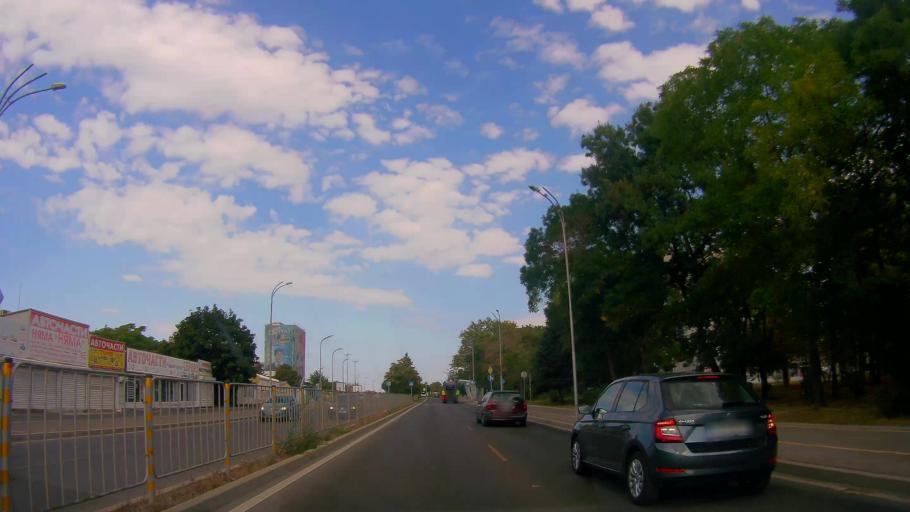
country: BG
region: Burgas
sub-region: Obshtina Burgas
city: Burgas
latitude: 42.5189
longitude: 27.4434
